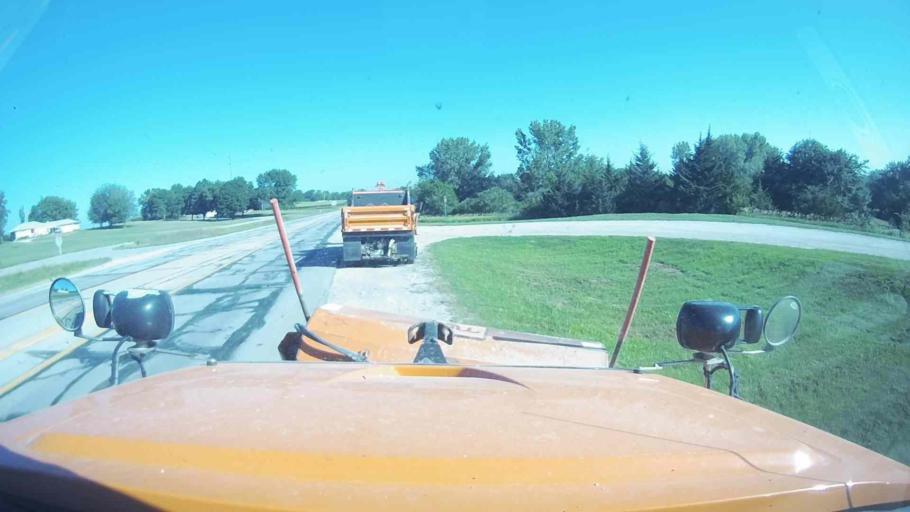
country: US
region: Iowa
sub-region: Cherokee County
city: Cherokee
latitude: 42.7744
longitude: -95.5565
